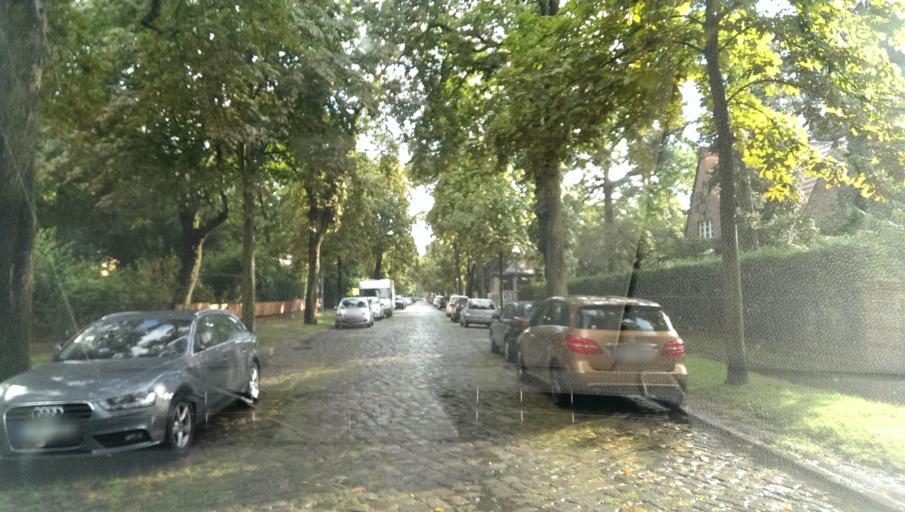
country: DE
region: Berlin
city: Lichterfelde
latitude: 52.4317
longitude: 13.3233
